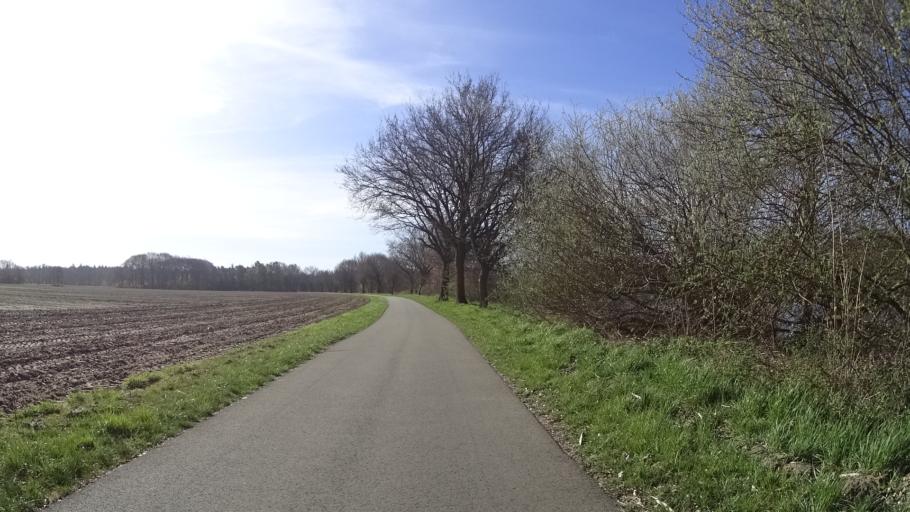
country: DE
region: Lower Saxony
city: Meppen
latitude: 52.7197
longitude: 7.2680
